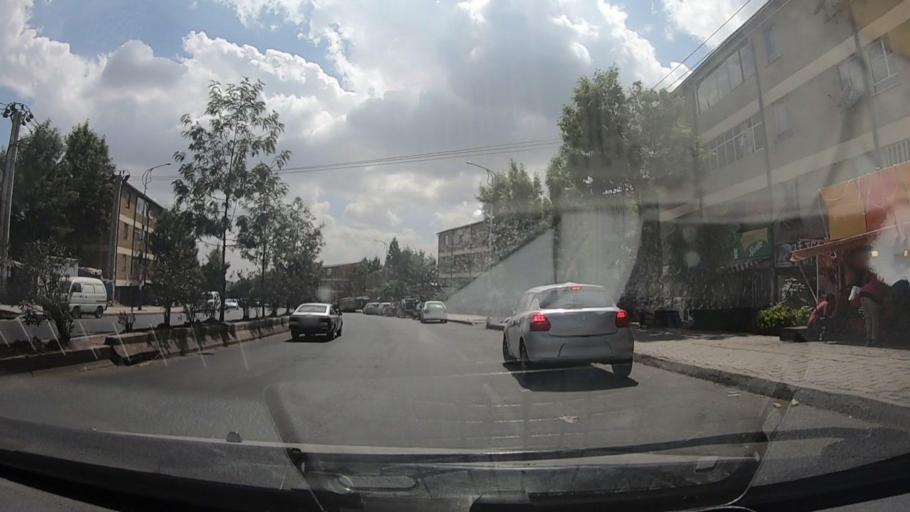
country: ET
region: Adis Abeba
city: Addis Ababa
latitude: 8.9772
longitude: 38.7220
